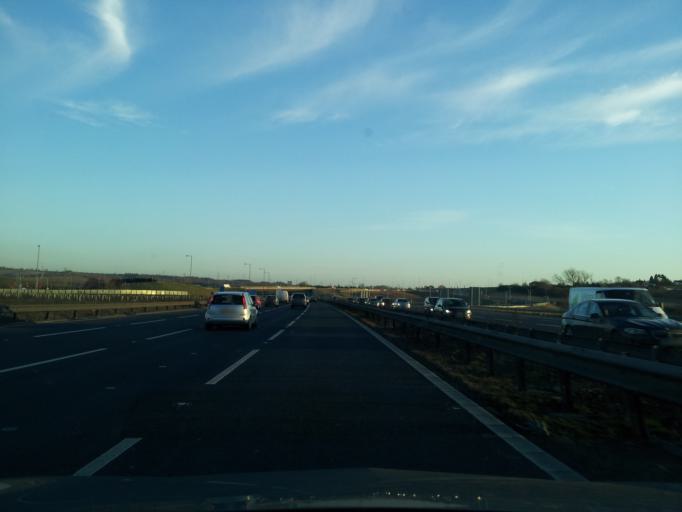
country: GB
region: England
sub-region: Central Bedfordshire
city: Toddington
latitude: 51.9621
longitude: -0.5210
